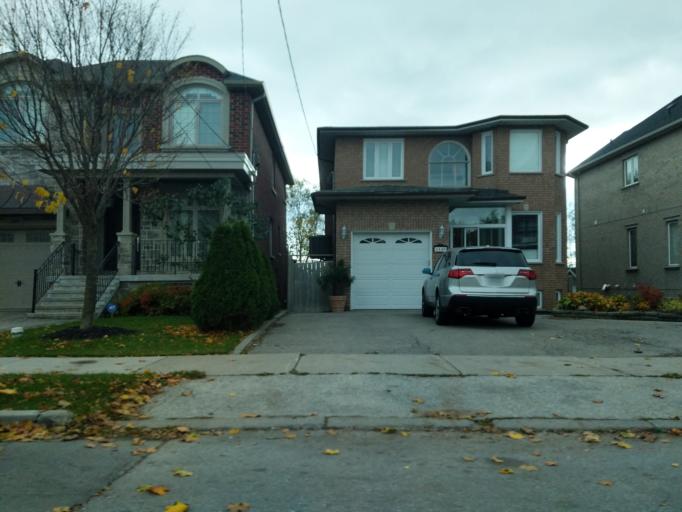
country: CA
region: Ontario
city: Toronto
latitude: 43.7058
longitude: -79.4598
